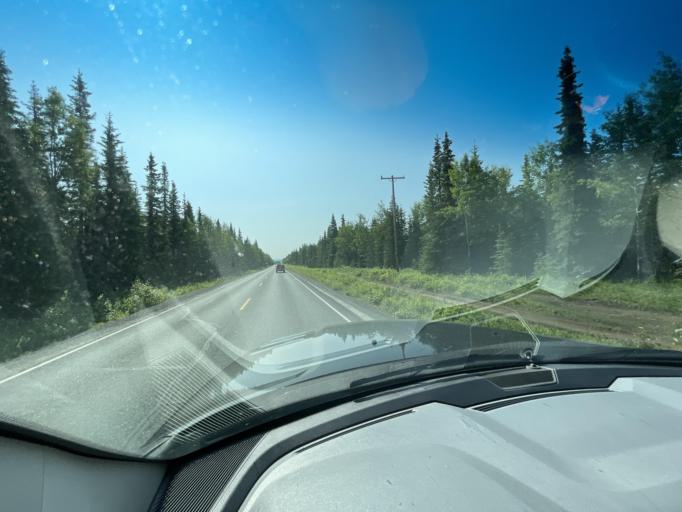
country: US
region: Alaska
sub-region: Kenai Peninsula Borough
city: Cohoe
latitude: 60.3107
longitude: -151.2916
